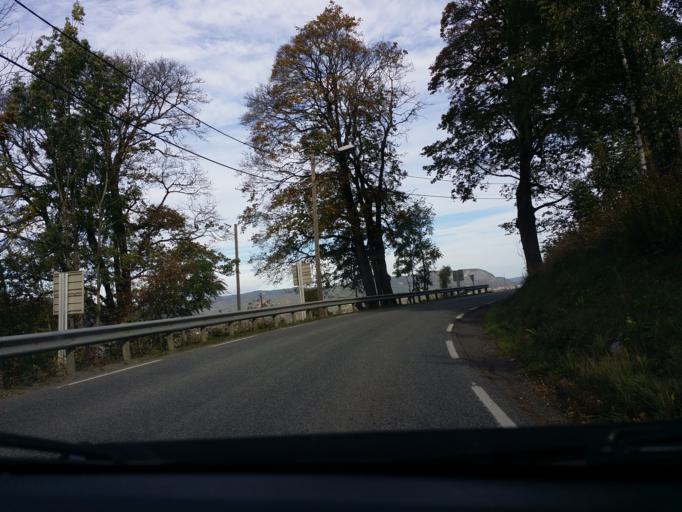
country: NO
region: Buskerud
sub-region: Lier
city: Tranby
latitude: 59.8377
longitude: 10.2607
